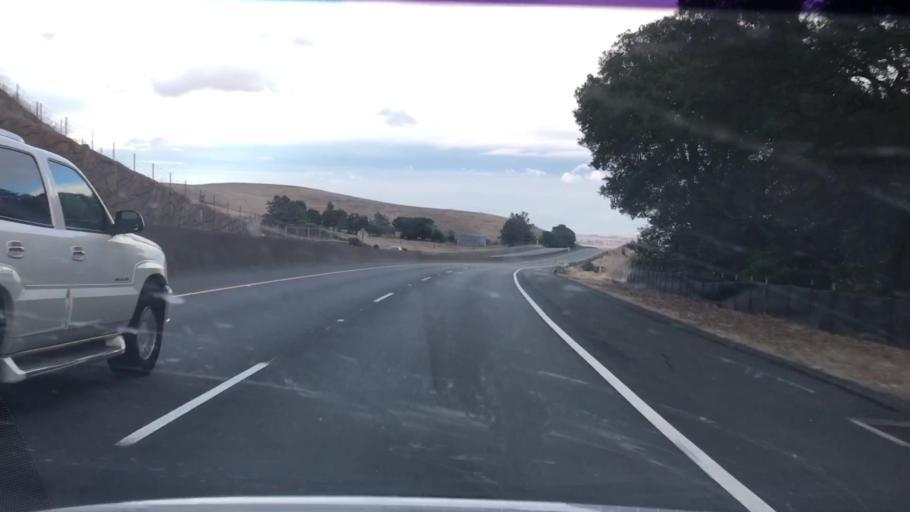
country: US
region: California
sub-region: Solano County
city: Green Valley
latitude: 38.2075
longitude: -122.1701
